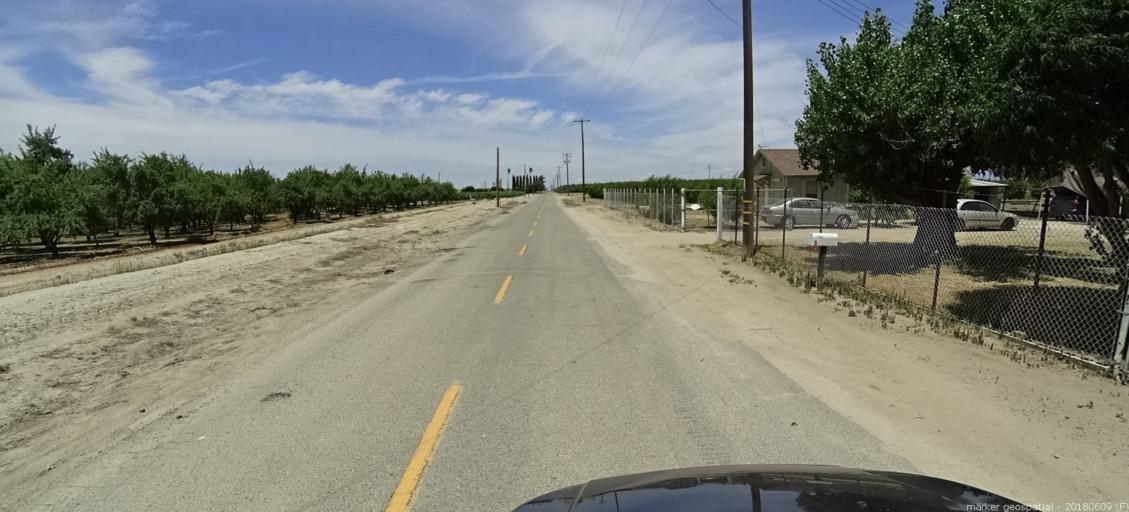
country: US
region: California
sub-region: Madera County
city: Parkwood
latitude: 36.9133
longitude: -120.1015
